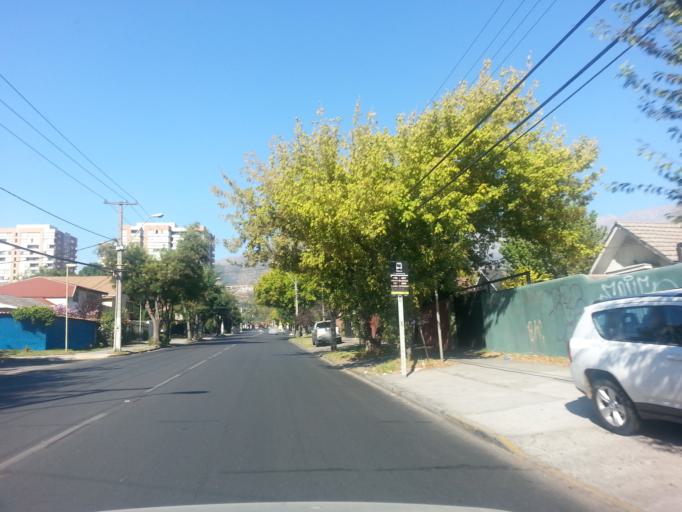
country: CL
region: Santiago Metropolitan
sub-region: Provincia de Santiago
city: Villa Presidente Frei, Nunoa, Santiago, Chile
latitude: -33.4243
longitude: -70.5426
